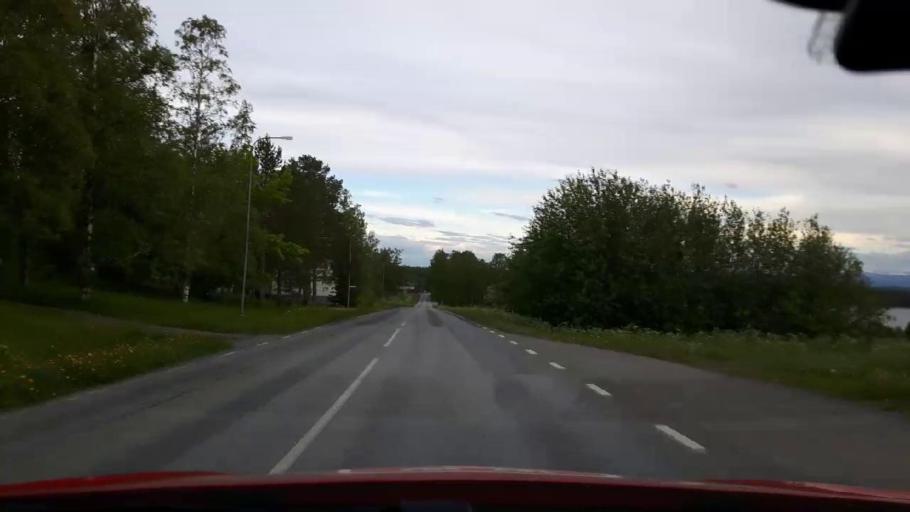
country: SE
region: Jaemtland
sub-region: OEstersunds Kommun
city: Ostersund
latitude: 63.1331
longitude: 14.4561
